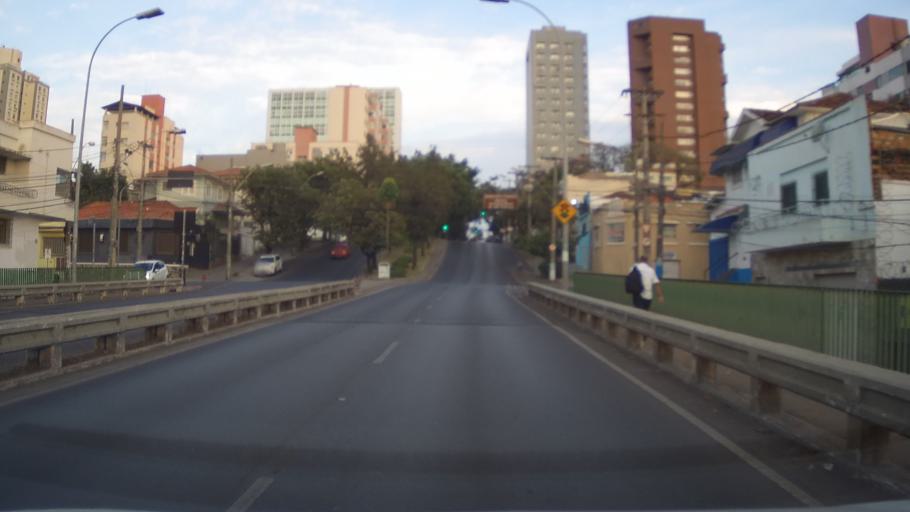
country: BR
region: Minas Gerais
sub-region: Belo Horizonte
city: Belo Horizonte
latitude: -19.9197
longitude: -43.9294
